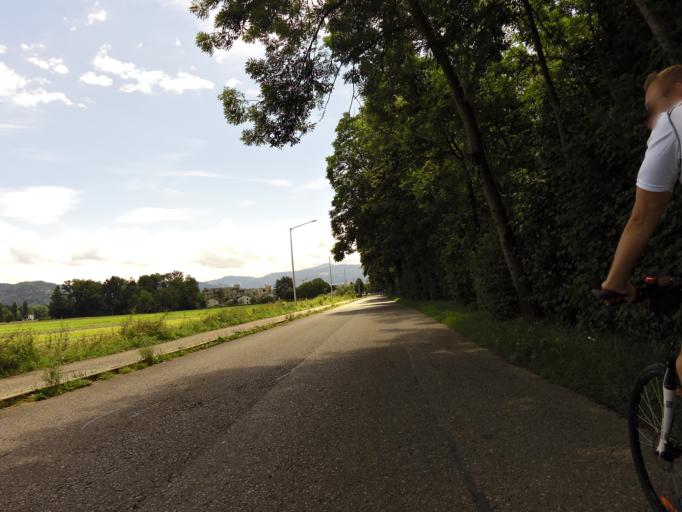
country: AT
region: Vorarlberg
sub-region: Politischer Bezirk Bregenz
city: Hard
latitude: 47.5023
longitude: 9.7030
